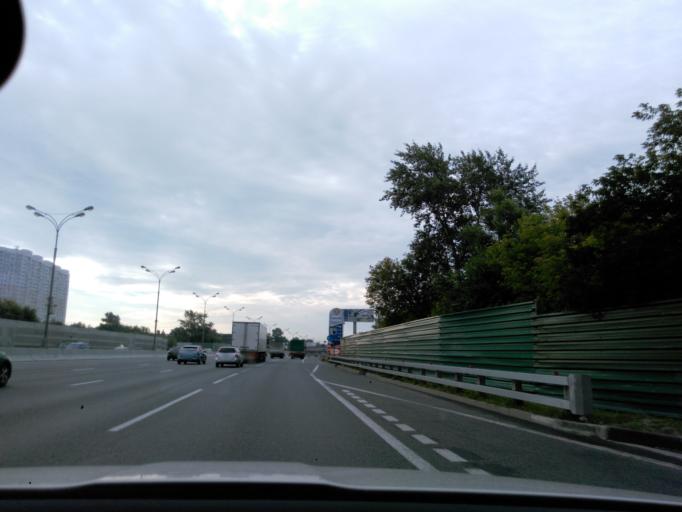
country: RU
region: Moscow
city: Vatutino
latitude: 55.8927
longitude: 37.7036
